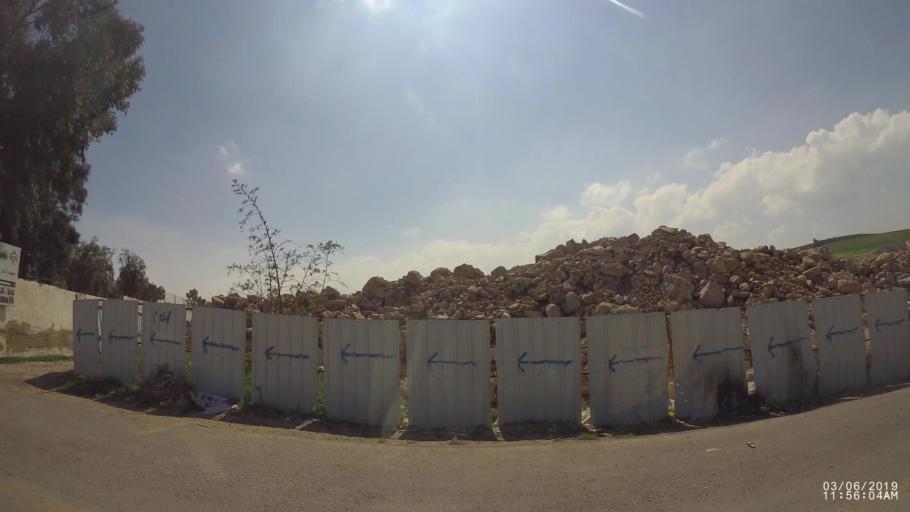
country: JO
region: Zarqa
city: Russeifa
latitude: 31.9841
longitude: 36.0135
